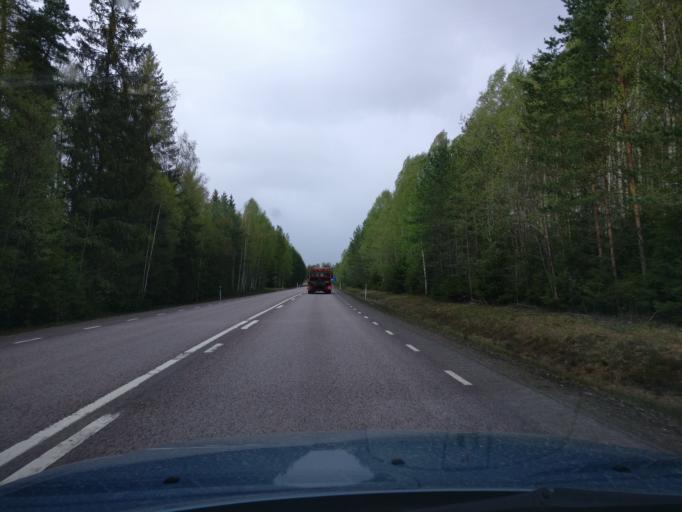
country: SE
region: Vaermland
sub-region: Forshaga Kommun
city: Deje
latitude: 59.6098
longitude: 13.4475
